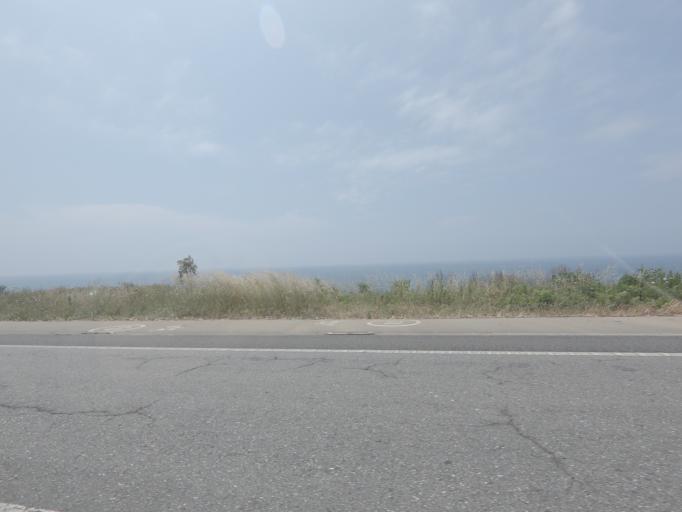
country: ES
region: Galicia
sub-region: Provincia de Pontevedra
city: A Guarda
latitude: 41.9298
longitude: -8.8817
